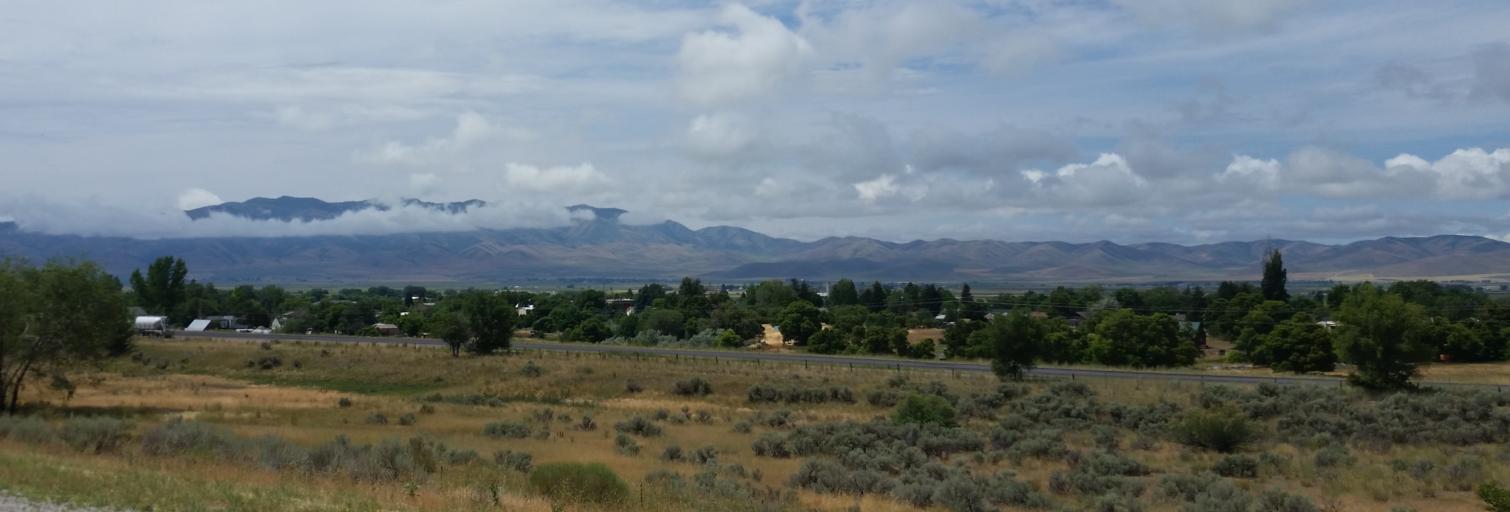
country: US
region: Idaho
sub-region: Oneida County
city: Malad City
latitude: 42.1921
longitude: -112.2367
